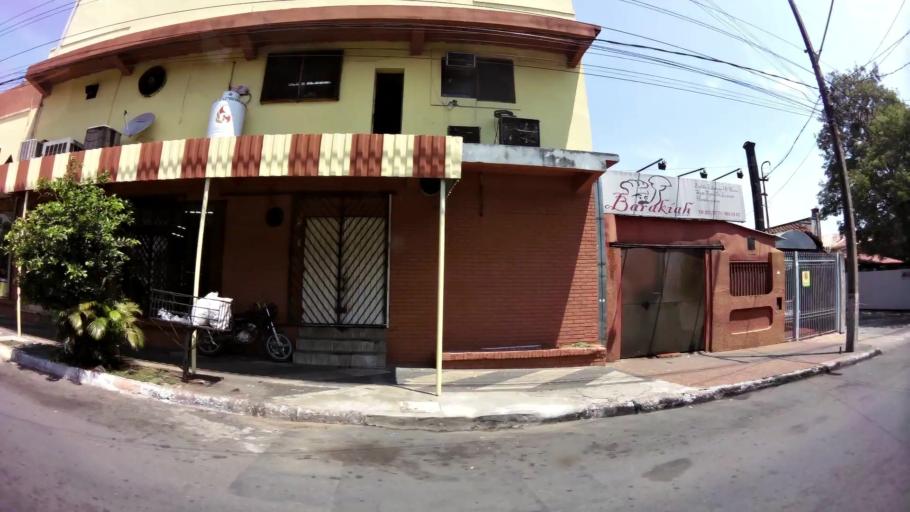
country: PY
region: Asuncion
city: Asuncion
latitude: -25.2991
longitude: -57.6335
